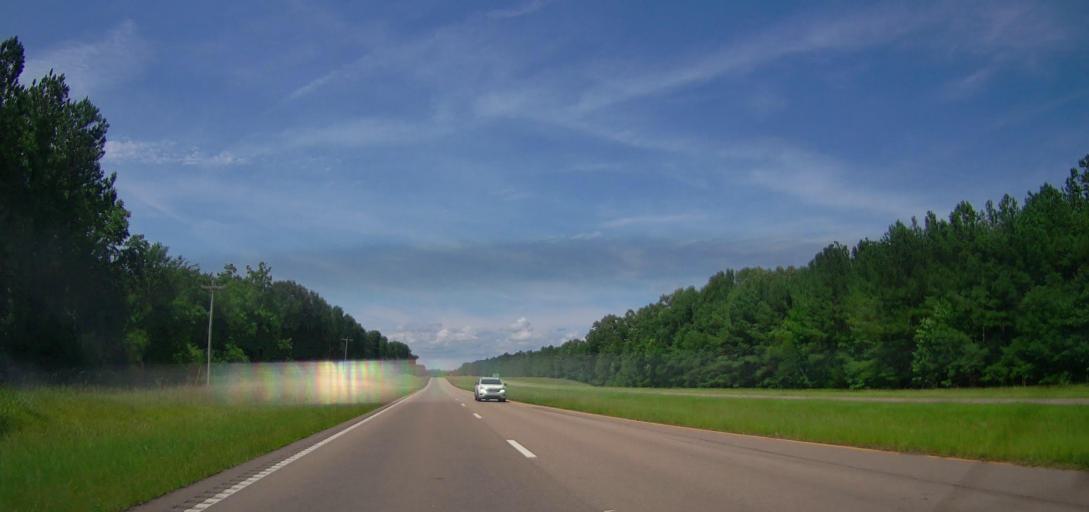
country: US
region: Mississippi
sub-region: Monroe County
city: Aberdeen
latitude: 33.9149
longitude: -88.5963
